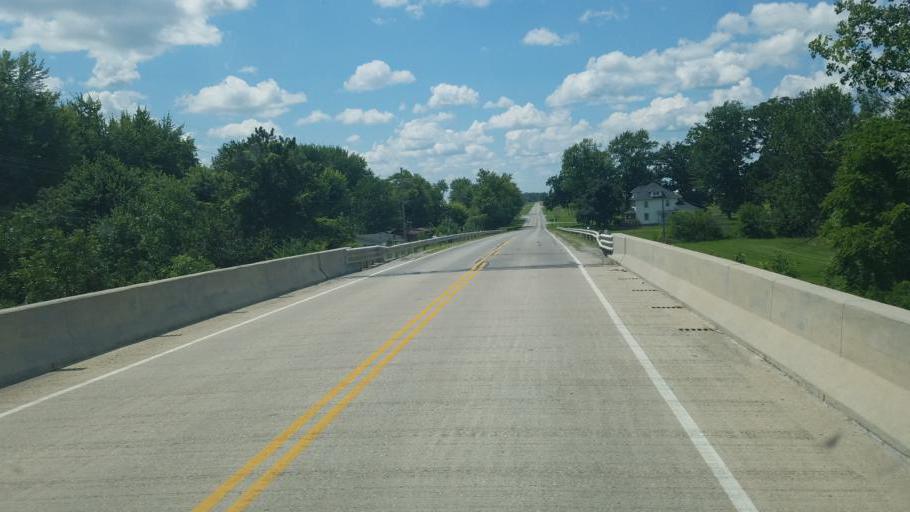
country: US
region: Ohio
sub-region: Marion County
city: Marion
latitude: 40.6298
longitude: -83.0971
